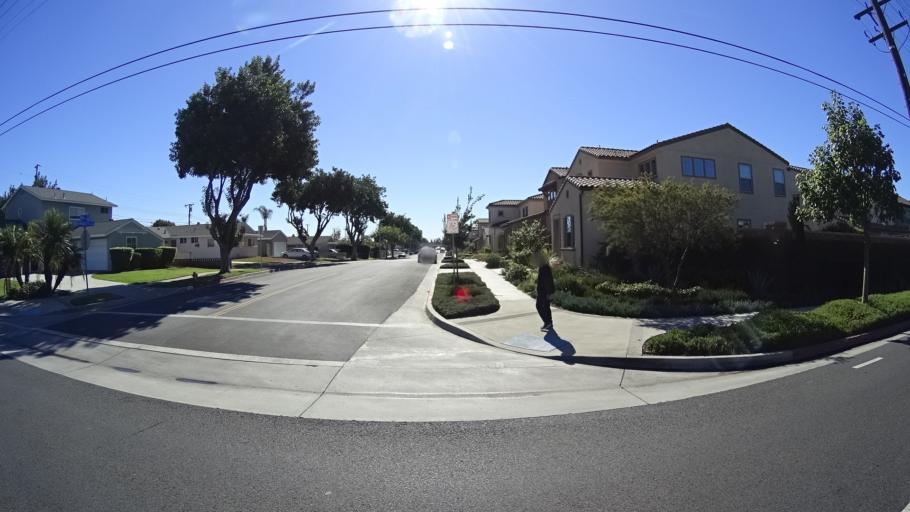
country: US
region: California
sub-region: Orange County
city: Cypress
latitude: 33.8171
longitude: -118.0223
